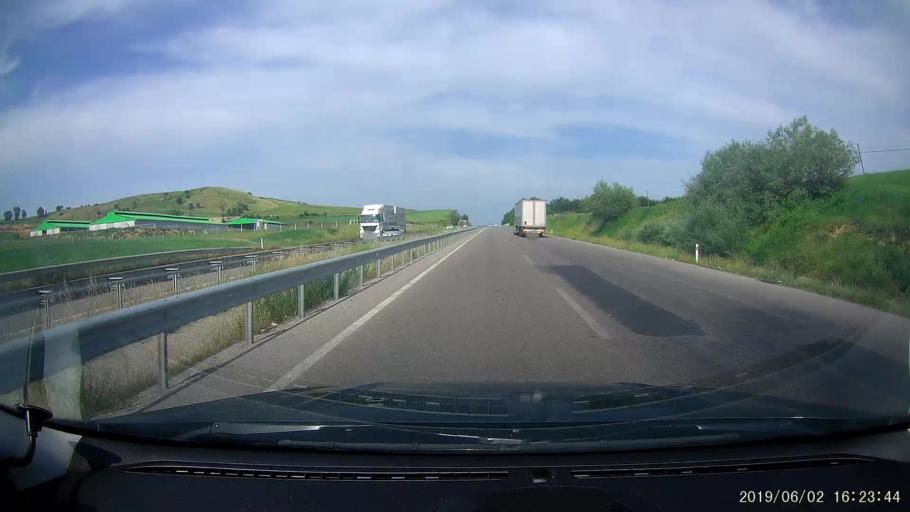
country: TR
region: Samsun
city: Havza
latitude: 40.9955
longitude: 35.7418
